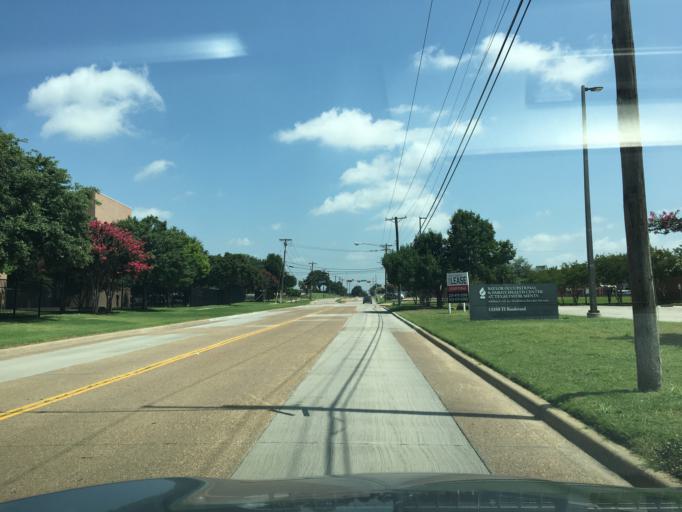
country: US
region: Texas
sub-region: Dallas County
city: Richardson
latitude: 32.9293
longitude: -96.7489
